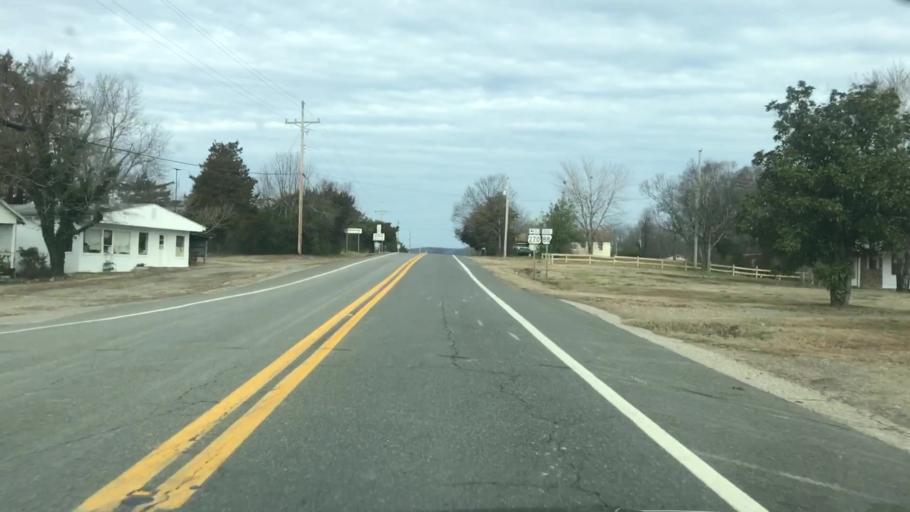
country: US
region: Arkansas
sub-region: Montgomery County
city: Mount Ida
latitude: 34.6300
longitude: -93.7341
